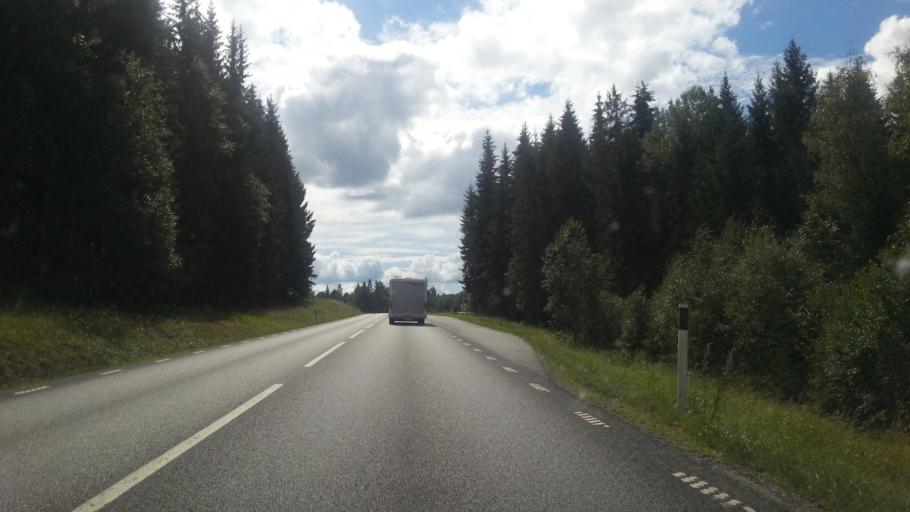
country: SE
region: OErebro
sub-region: Lindesbergs Kommun
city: Stora
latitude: 59.6749
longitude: 15.1000
